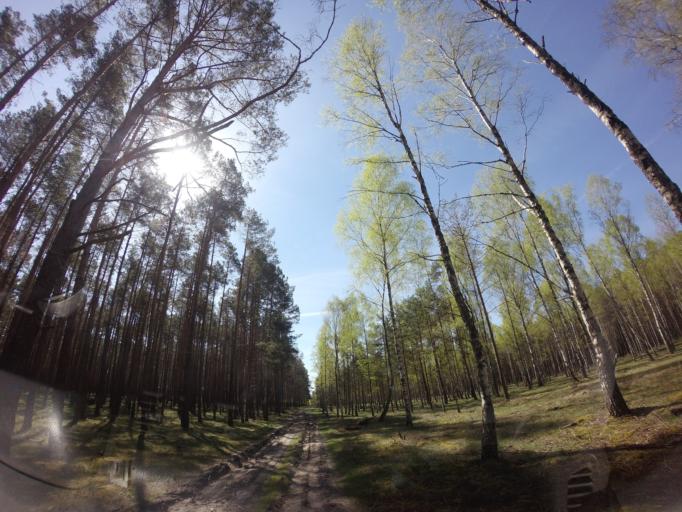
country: PL
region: West Pomeranian Voivodeship
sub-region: Powiat drawski
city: Kalisz Pomorski
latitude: 53.1949
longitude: 15.9396
